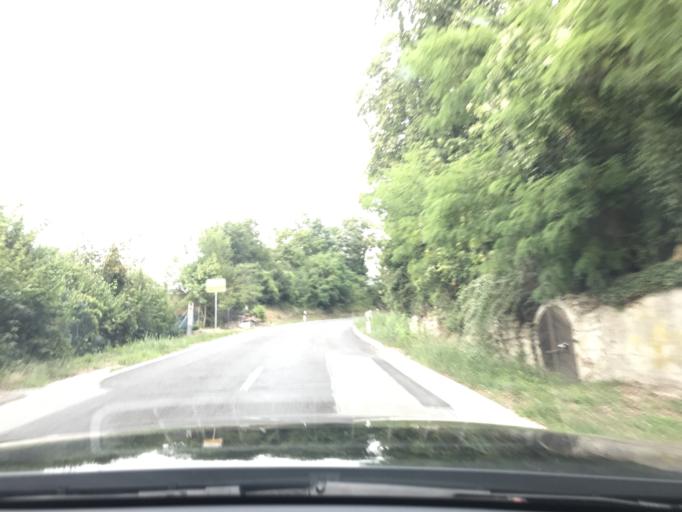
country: DE
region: Bavaria
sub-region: Regierungsbezirk Unterfranken
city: Zeil
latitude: 50.0104
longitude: 10.5982
